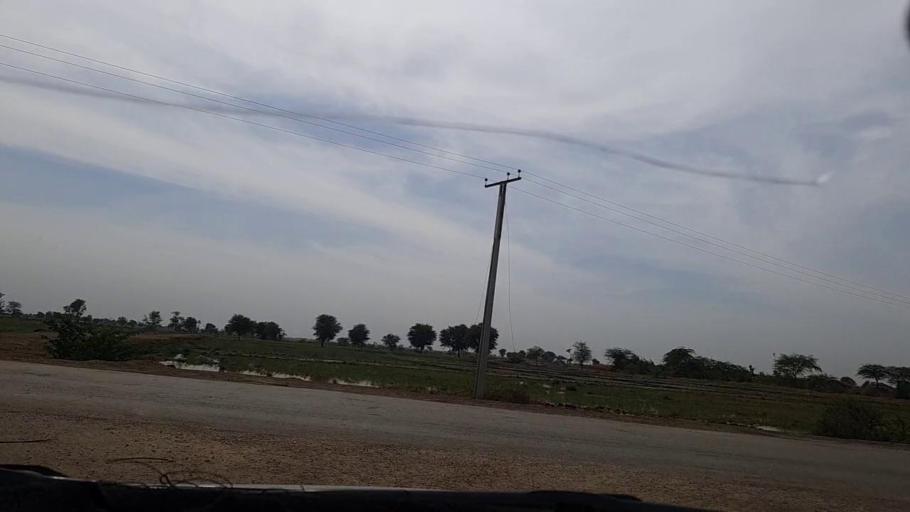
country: PK
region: Sindh
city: Dhoro Naro
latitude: 25.4416
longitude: 69.4918
